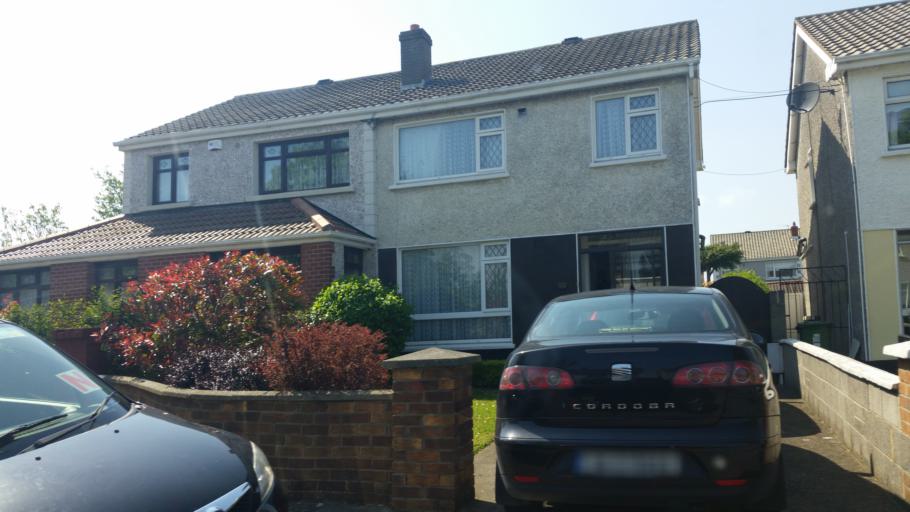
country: IE
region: Leinster
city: Donaghmede
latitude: 53.3976
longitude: -6.1649
